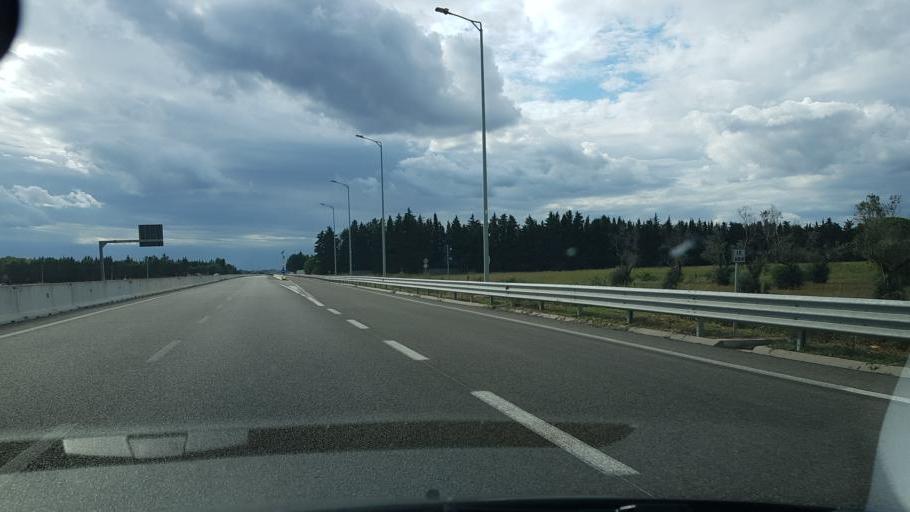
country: IT
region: Apulia
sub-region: Provincia di Lecce
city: Palmariggi
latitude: 40.1274
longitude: 18.3575
